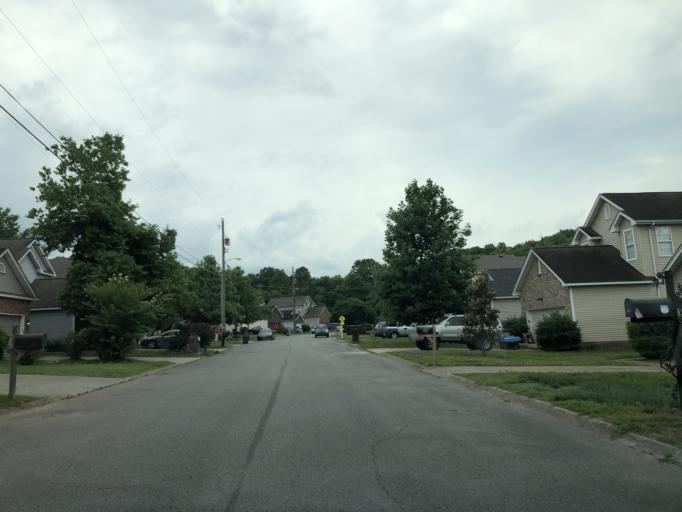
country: US
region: Tennessee
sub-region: Davidson County
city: Goodlettsville
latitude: 36.2533
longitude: -86.7661
